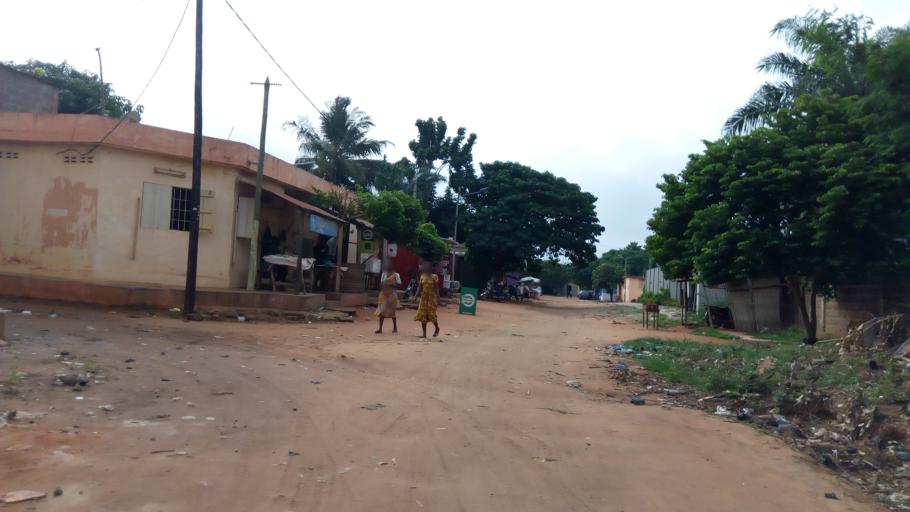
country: TG
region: Maritime
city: Lome
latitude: 6.1829
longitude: 1.1925
